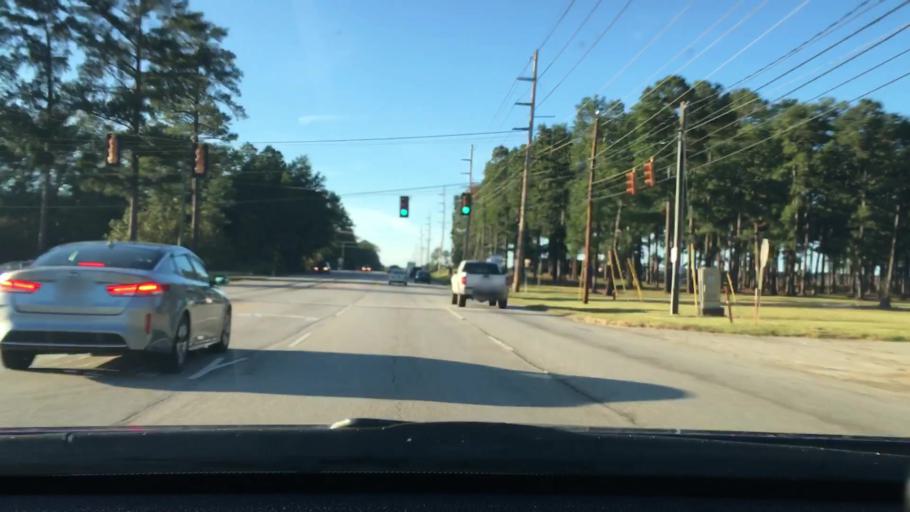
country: US
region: South Carolina
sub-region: Lexington County
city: Saint Andrews
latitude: 34.0706
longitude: -81.1200
